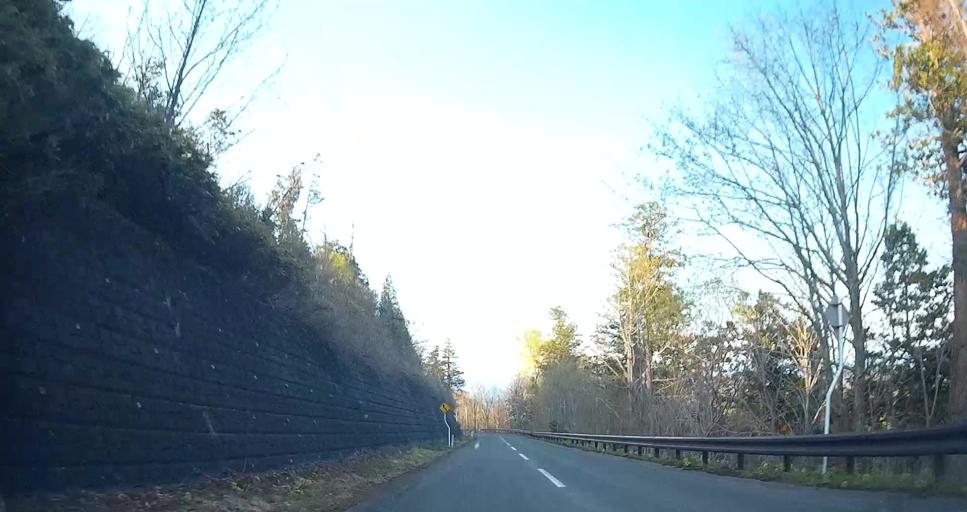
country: JP
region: Aomori
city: Mutsu
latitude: 41.3135
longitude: 141.1091
